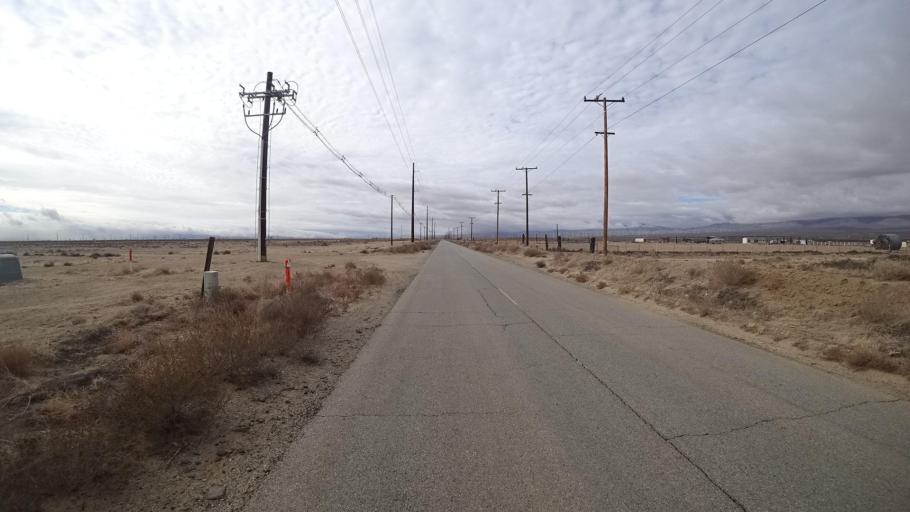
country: US
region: California
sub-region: Kern County
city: Rosamond
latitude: 34.8632
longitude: -118.3351
